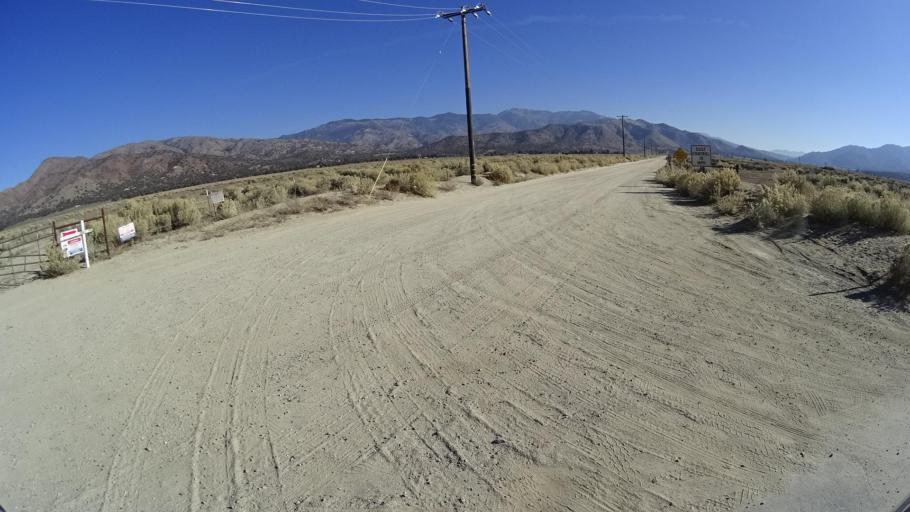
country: US
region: California
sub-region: Kern County
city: Bodfish
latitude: 35.4129
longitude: -118.5235
